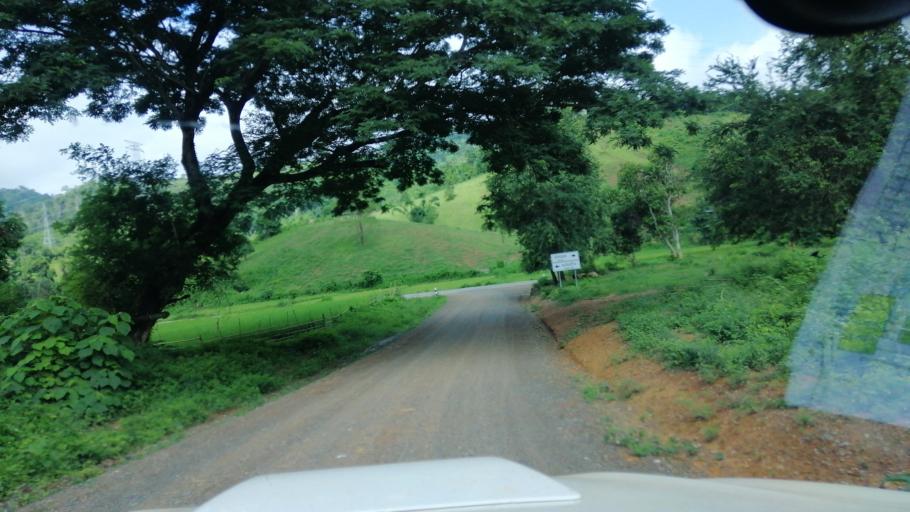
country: LA
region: Xiagnabouli
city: Muang Kenthao
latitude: 17.9122
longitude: 101.3513
